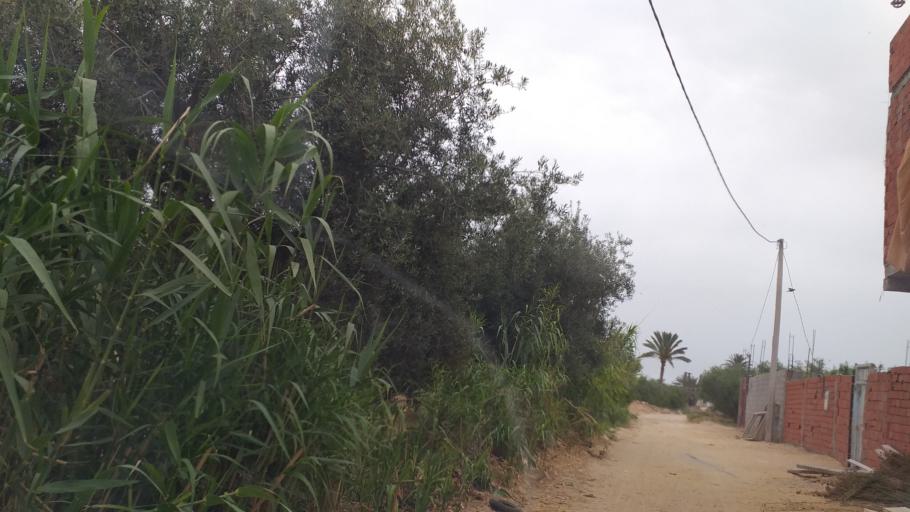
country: TN
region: Qabis
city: Gabes
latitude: 33.9549
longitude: 10.0598
